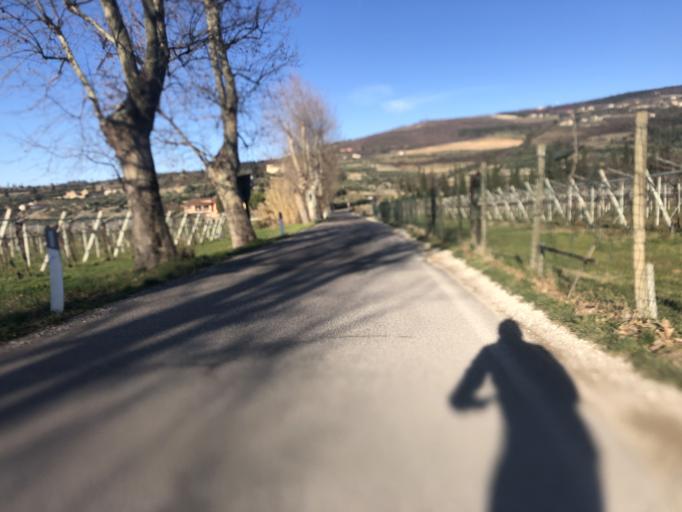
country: IT
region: Veneto
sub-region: Provincia di Verona
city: Fumane
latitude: 45.5335
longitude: 10.8841
